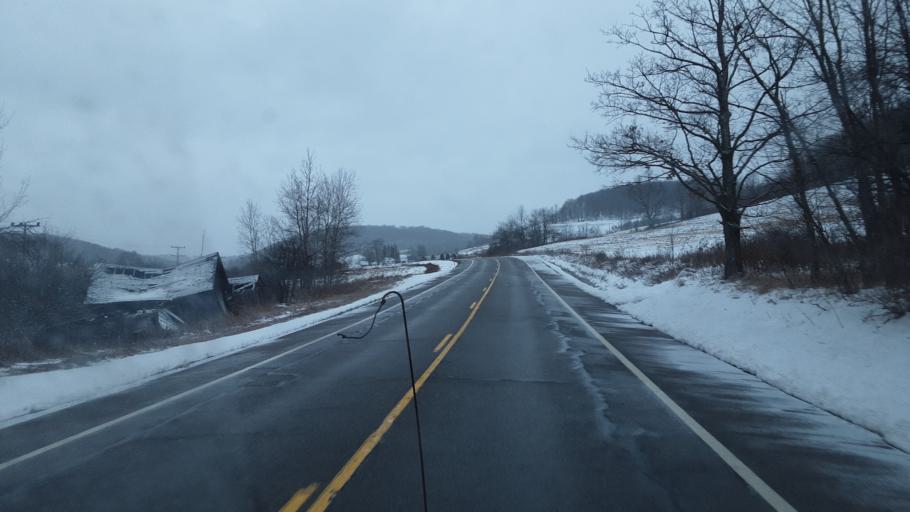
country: US
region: Pennsylvania
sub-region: Tioga County
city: Westfield
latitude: 42.0723
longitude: -77.5475
